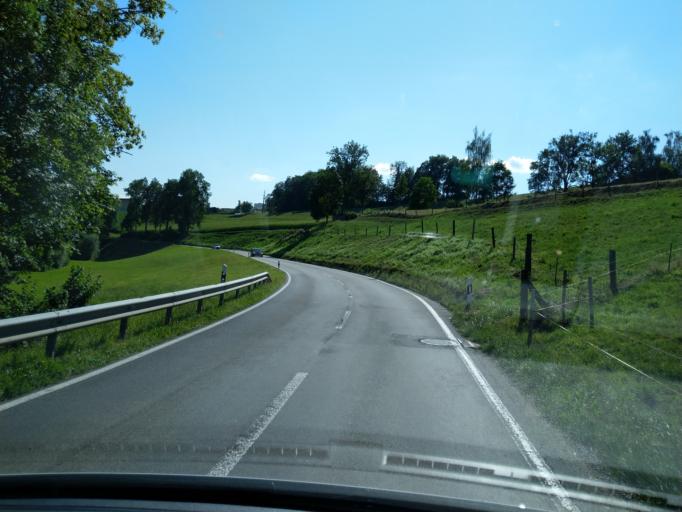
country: CH
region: Lucerne
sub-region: Entlebuch District
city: Werthenstein
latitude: 47.0682
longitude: 8.0986
